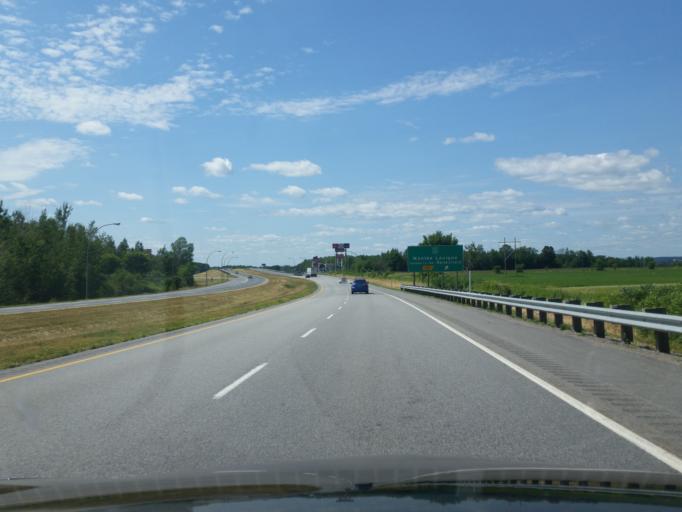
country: CA
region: Quebec
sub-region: Monteregie
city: Hudson
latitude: 45.4566
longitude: -74.2197
